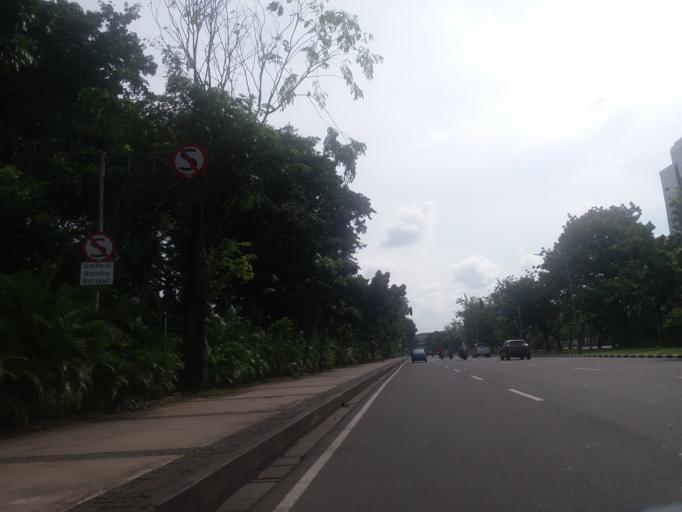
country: ID
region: Jakarta Raya
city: Jakarta
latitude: -6.1716
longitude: 106.8284
